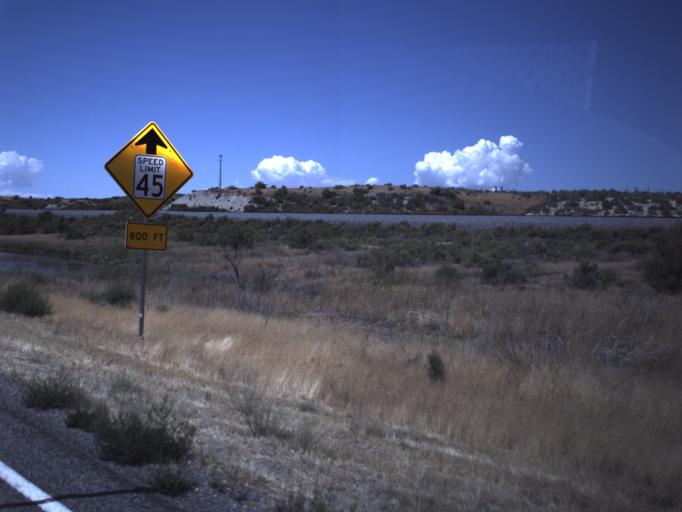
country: US
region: Utah
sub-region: Millard County
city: Delta
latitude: 39.5267
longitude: -112.3570
